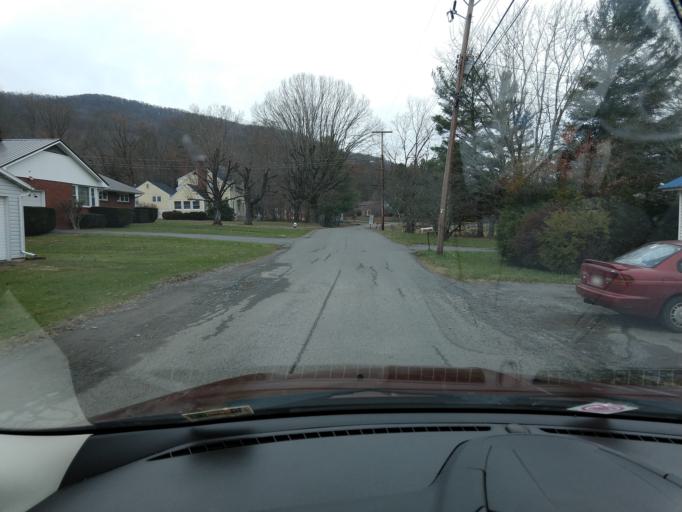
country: US
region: West Virginia
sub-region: Greenbrier County
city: Rainelle
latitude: 37.9642
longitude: -80.6891
